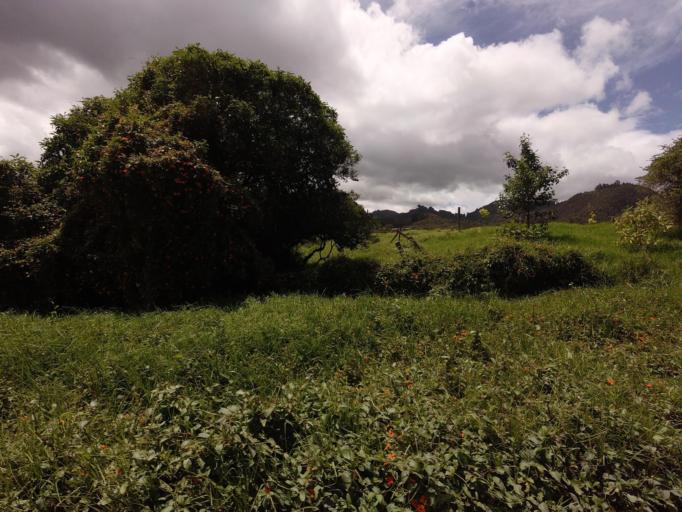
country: CO
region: Cundinamarca
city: Tabio
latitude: 4.9318
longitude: -74.0712
